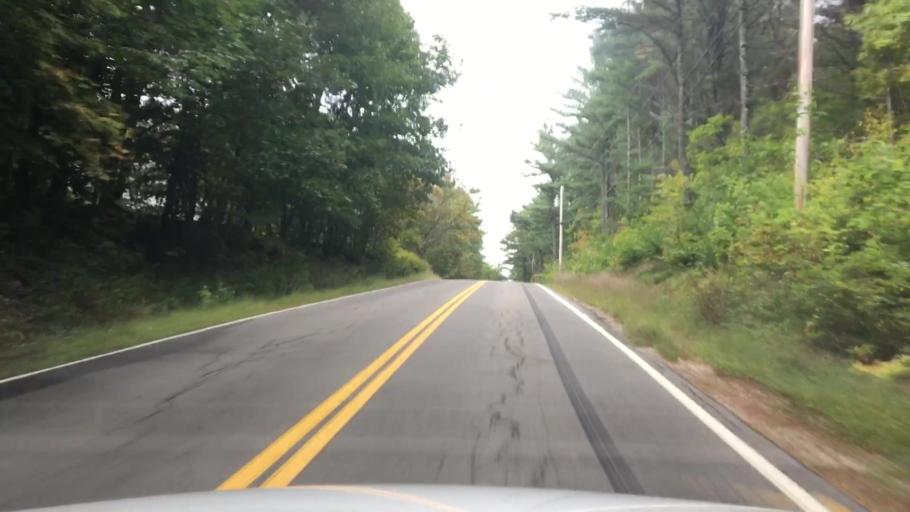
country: US
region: New Hampshire
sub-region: Carroll County
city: Effingham
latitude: 43.7414
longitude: -71.0081
